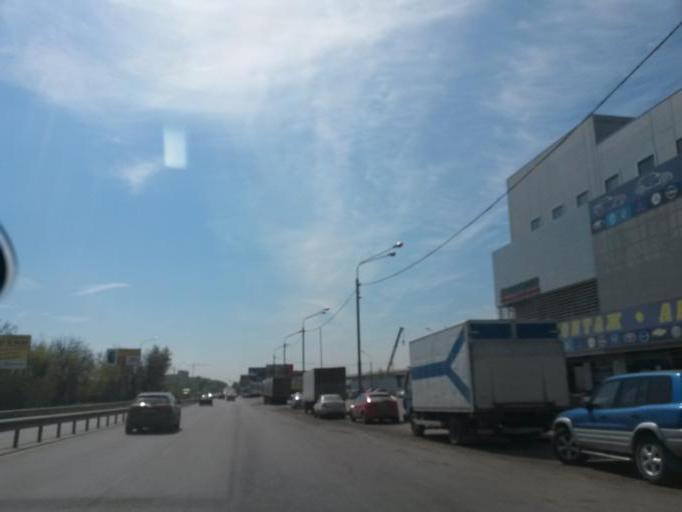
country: RU
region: Moskovskaya
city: Shcherbinka
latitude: 55.4973
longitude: 37.5702
